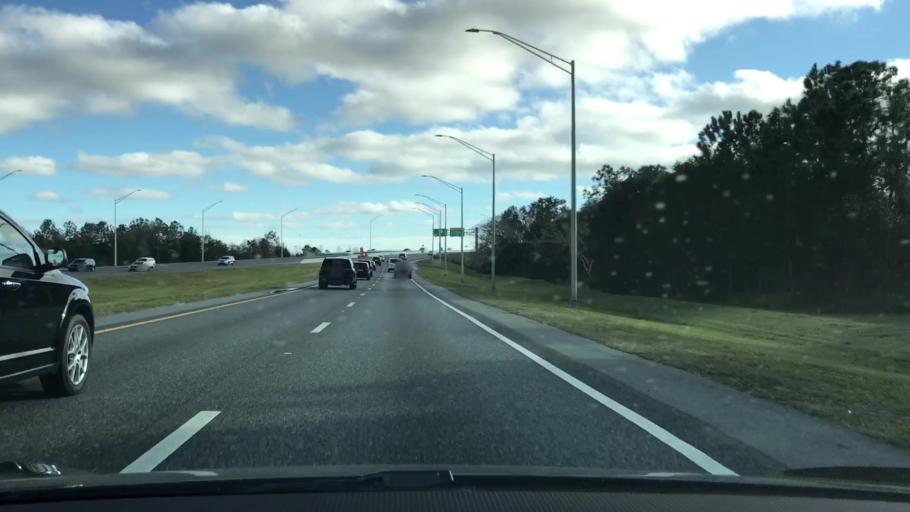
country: US
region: Florida
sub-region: Orange County
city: Meadow Woods
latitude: 28.3877
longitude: -81.3096
